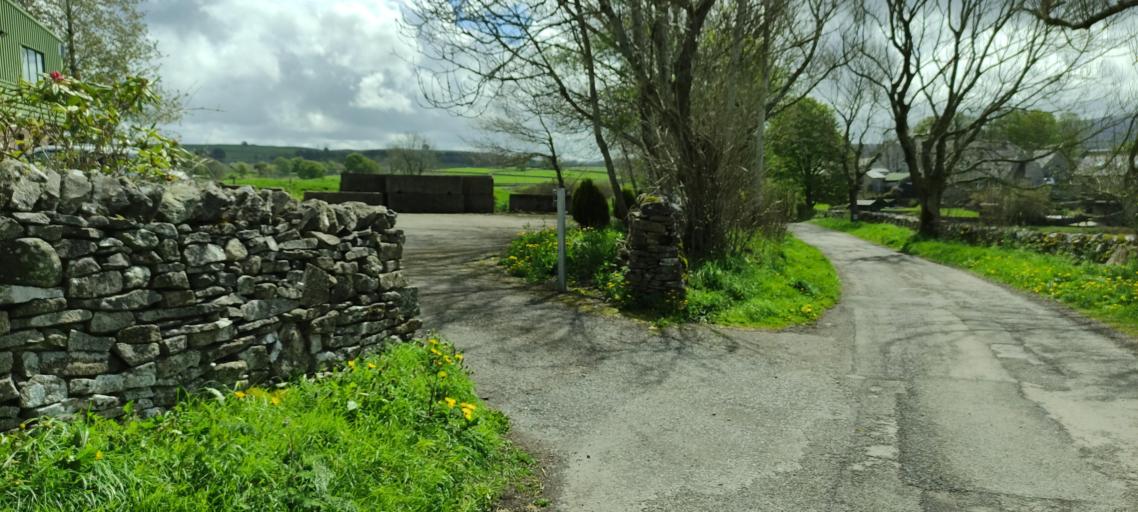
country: GB
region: England
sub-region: Cumbria
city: Penrith
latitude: 54.5224
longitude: -2.6749
